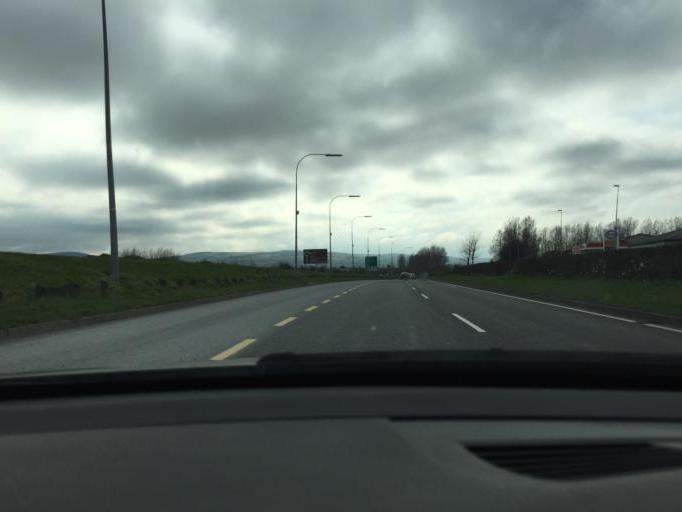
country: IE
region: Leinster
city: Firhouse
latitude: 53.2895
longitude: -6.3344
